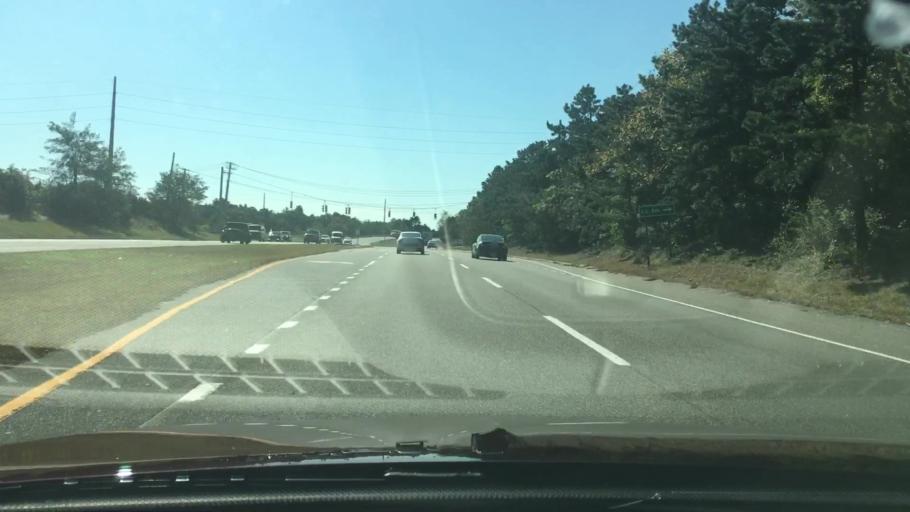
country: US
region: New York
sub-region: Suffolk County
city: Yaphank
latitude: 40.8263
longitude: -72.9400
